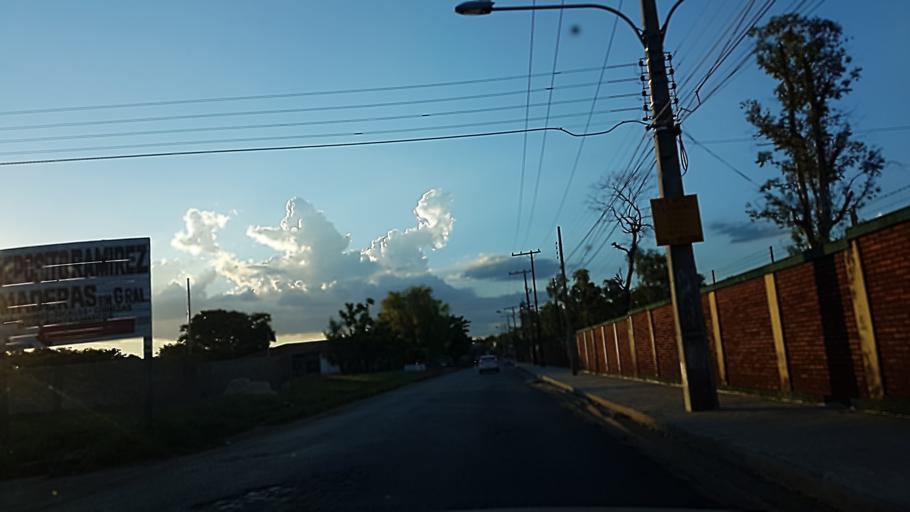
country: PY
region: Central
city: Colonia Mariano Roque Alonso
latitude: -25.2193
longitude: -57.5332
